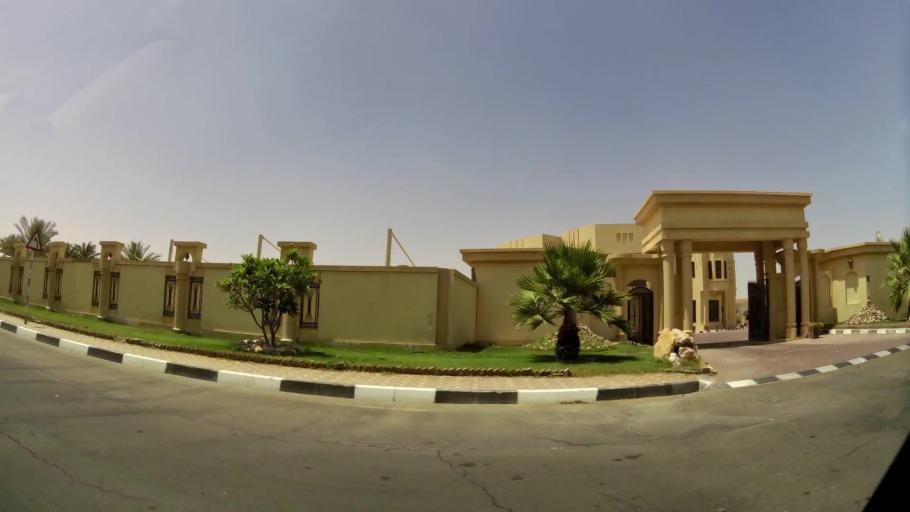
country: AE
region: Abu Dhabi
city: Al Ain
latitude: 24.2512
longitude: 55.7024
